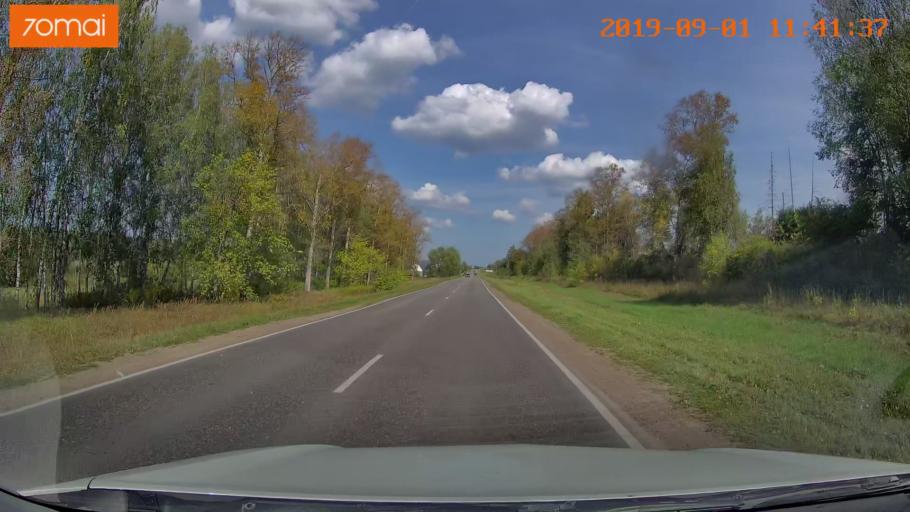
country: RU
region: Kaluga
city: Detchino
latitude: 54.8816
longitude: 36.3785
